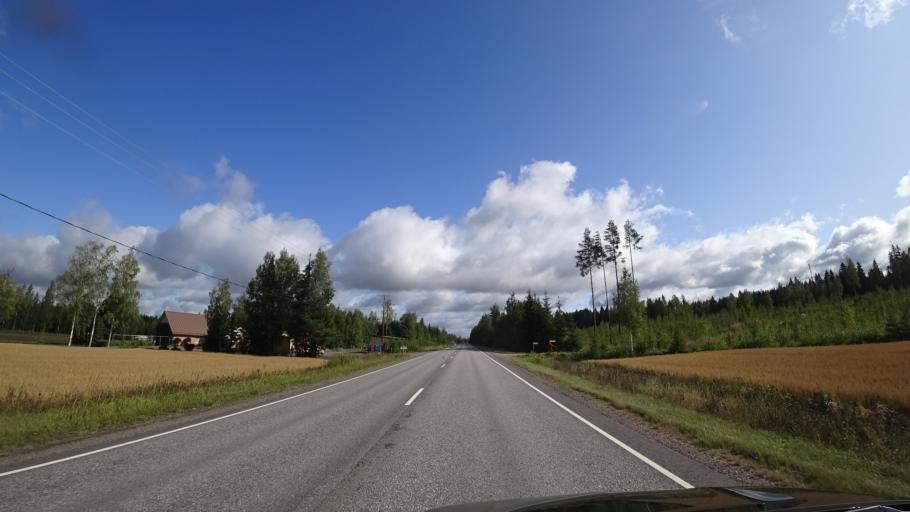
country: FI
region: Uusimaa
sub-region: Helsinki
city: Hyvinge
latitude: 60.5422
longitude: 24.9312
